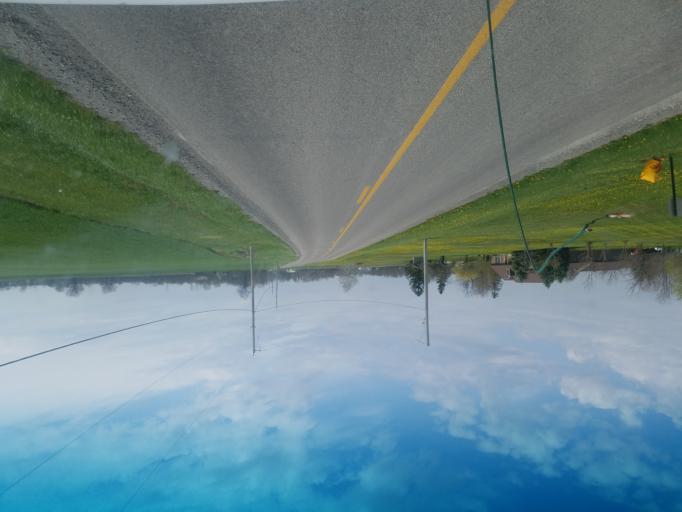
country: US
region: Ohio
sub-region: Logan County
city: Northwood
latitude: 40.4960
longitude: -83.7582
